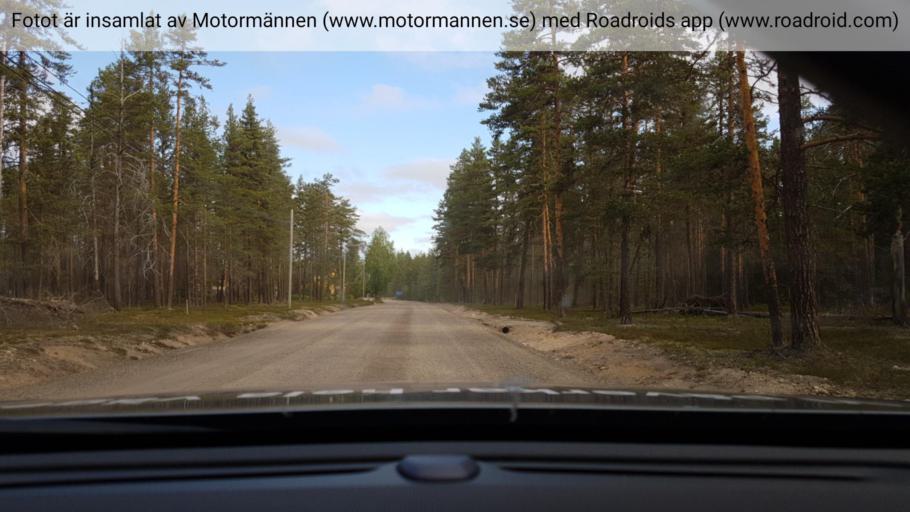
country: SE
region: Vaesterbotten
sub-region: Norsjo Kommun
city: Norsjoe
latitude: 64.6602
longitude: 19.2716
